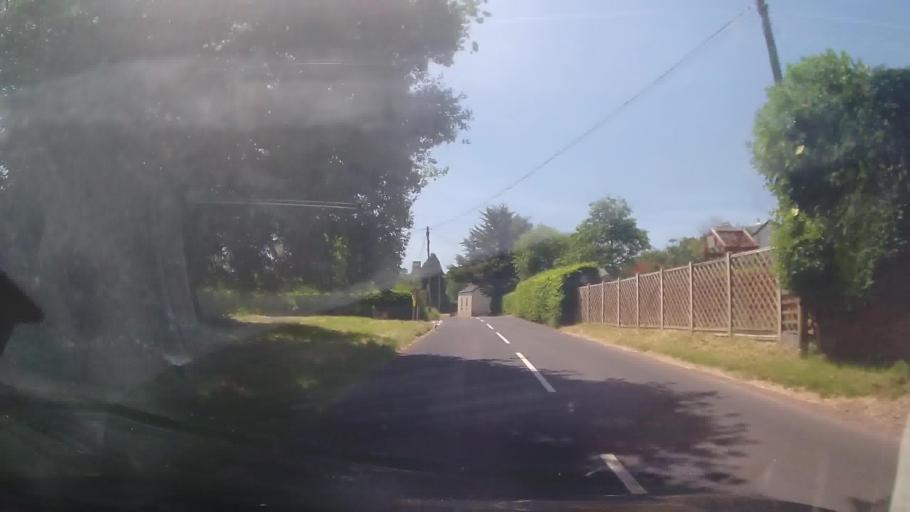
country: GB
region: England
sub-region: Herefordshire
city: Llanrothal
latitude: 51.8863
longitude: -2.7323
